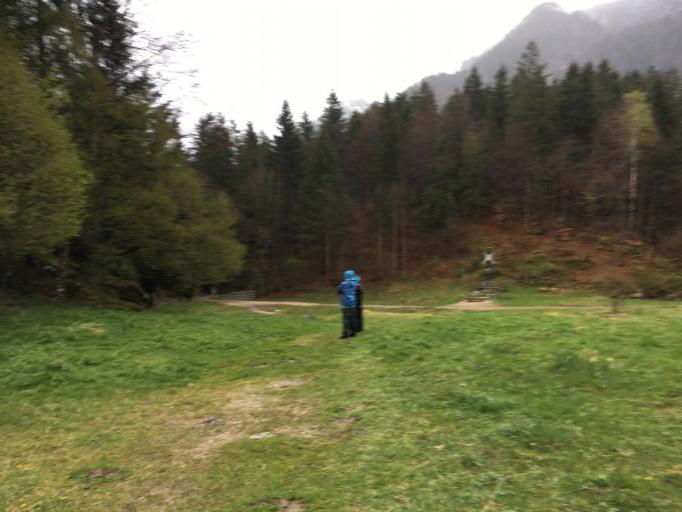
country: DE
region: Bavaria
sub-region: Upper Bavaria
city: Oberammergau
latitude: 47.5869
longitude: 11.0673
